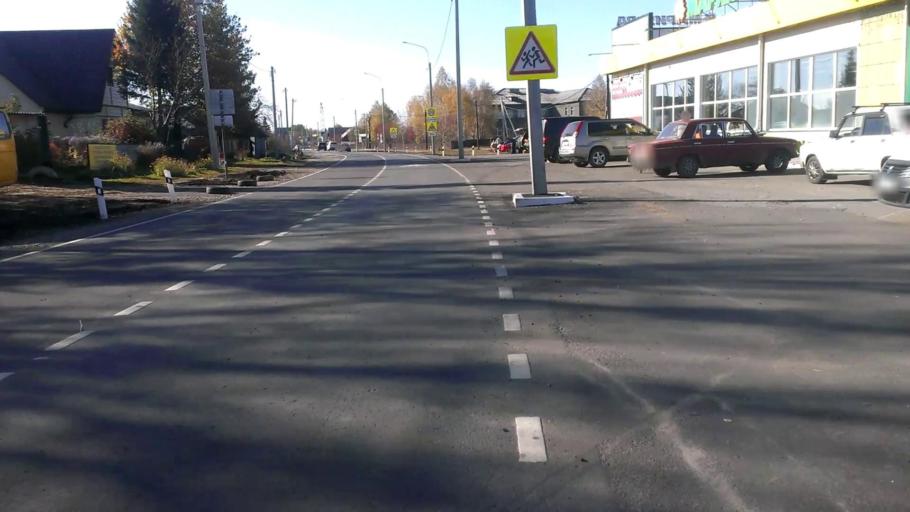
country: RU
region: Altai Krai
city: Sannikovo
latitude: 53.3169
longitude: 83.9565
